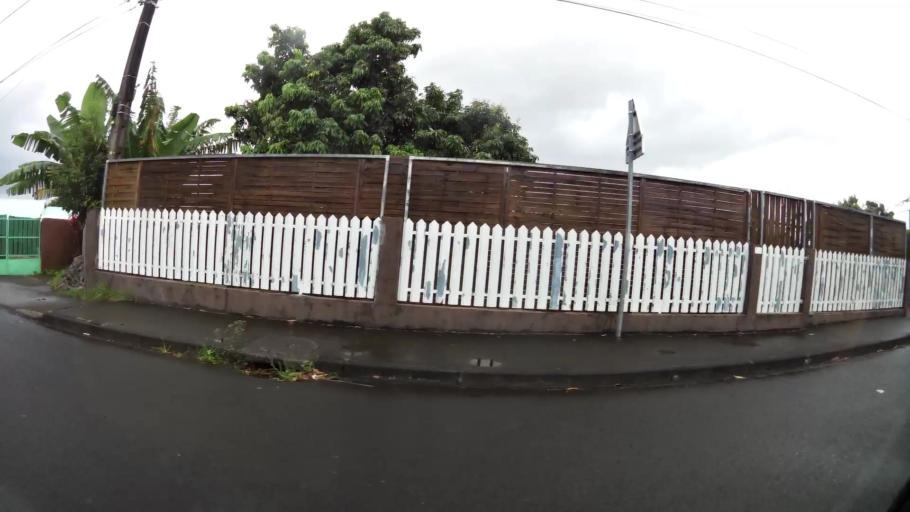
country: RE
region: Reunion
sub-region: Reunion
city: Saint-Andre
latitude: -20.9366
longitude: 55.6487
